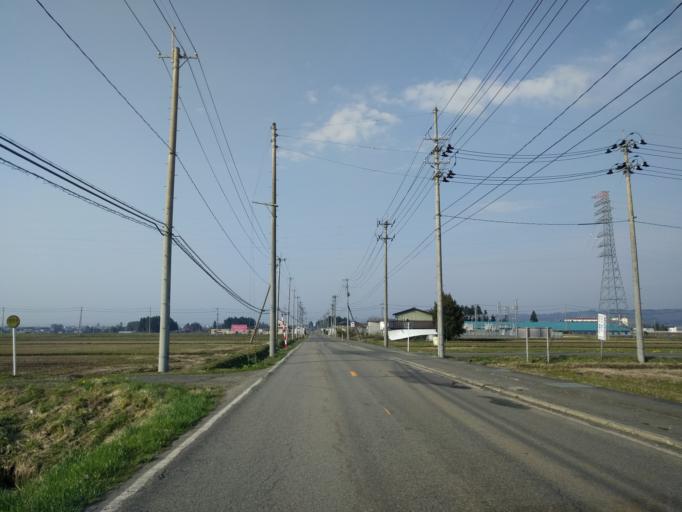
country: JP
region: Fukushima
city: Kitakata
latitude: 37.6753
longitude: 139.8934
